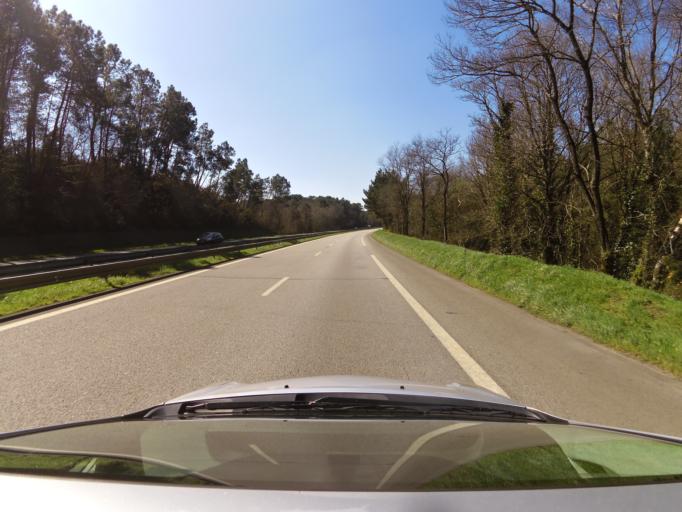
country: FR
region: Brittany
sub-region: Departement du Morbihan
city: Languidic
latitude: 47.8461
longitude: -3.1274
